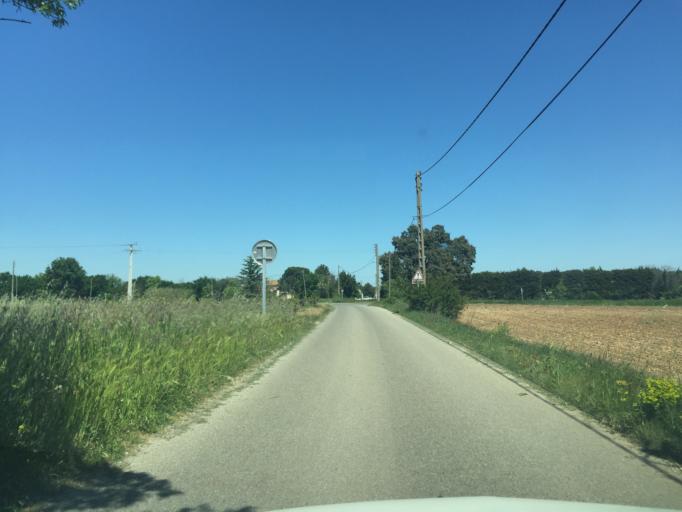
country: FR
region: Provence-Alpes-Cote d'Azur
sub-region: Departement du Vaucluse
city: Orange
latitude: 44.1104
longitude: 4.7996
